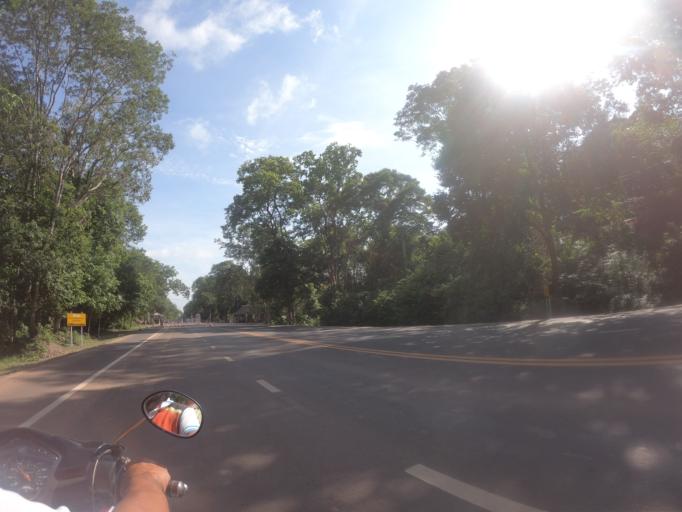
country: TH
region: Surin
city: Kap Choeng
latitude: 14.4397
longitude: 103.7007
